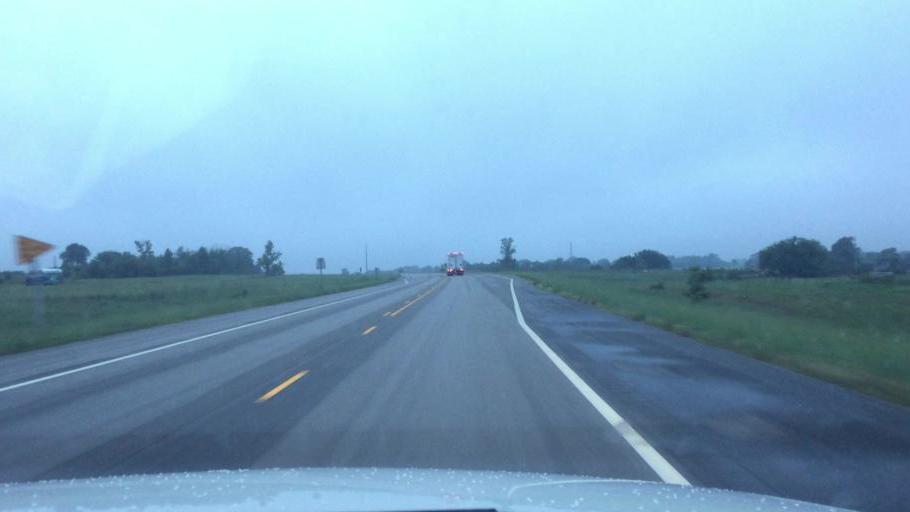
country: US
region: Kansas
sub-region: Montgomery County
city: Cherryvale
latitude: 37.4582
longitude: -95.4814
